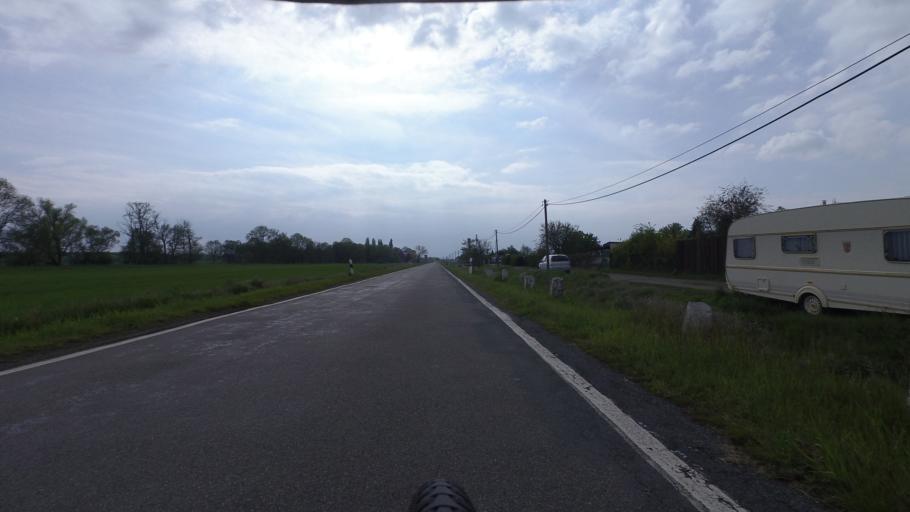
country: DE
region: Saxony-Anhalt
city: Langenstein
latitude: 51.8957
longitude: 11.0062
